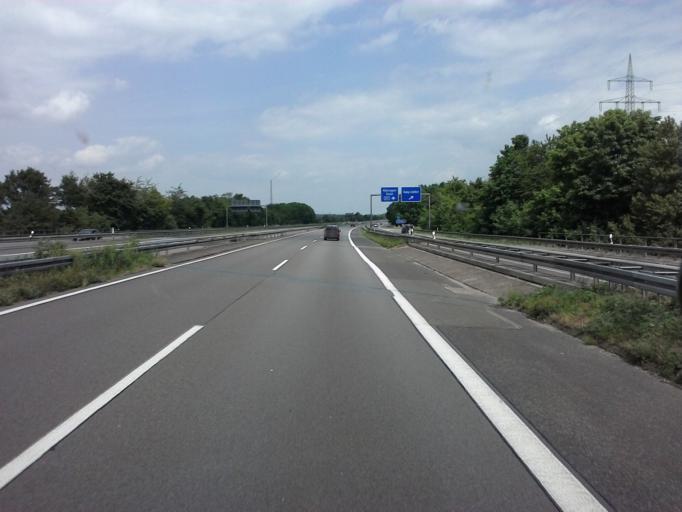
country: DE
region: North Rhine-Westphalia
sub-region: Regierungsbezirk Dusseldorf
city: Kamp-Lintfort
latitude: 51.4965
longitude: 6.5759
